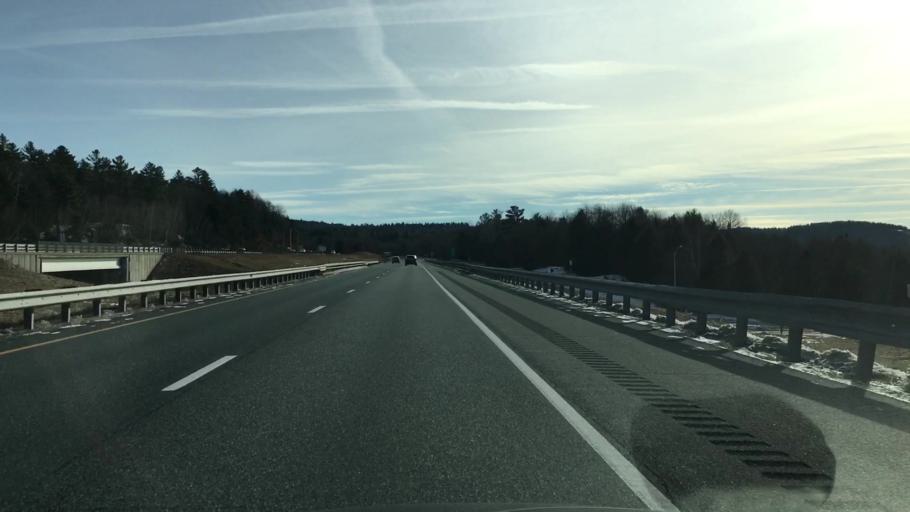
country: US
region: New Hampshire
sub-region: Sullivan County
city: Grantham
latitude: 43.4994
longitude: -72.1333
